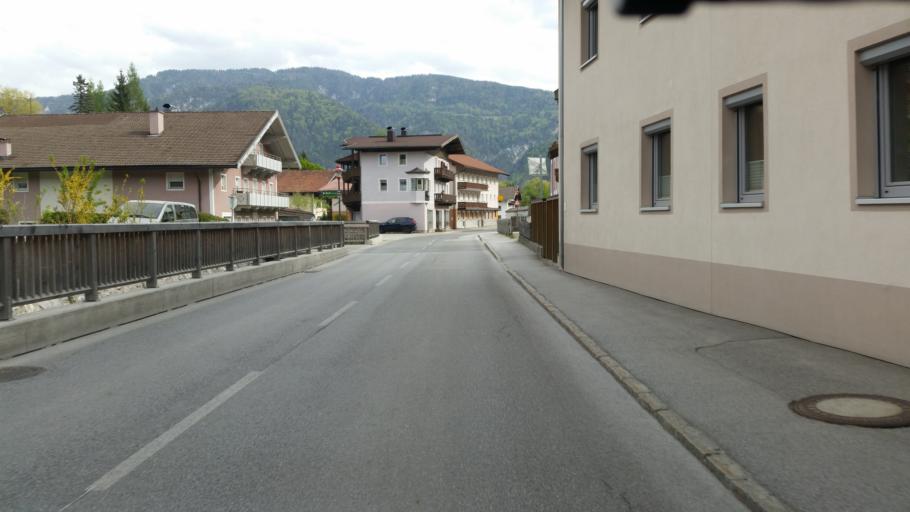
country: AT
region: Tyrol
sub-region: Politischer Bezirk Kufstein
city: Breitenbach am Inn
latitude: 47.4800
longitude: 11.9725
